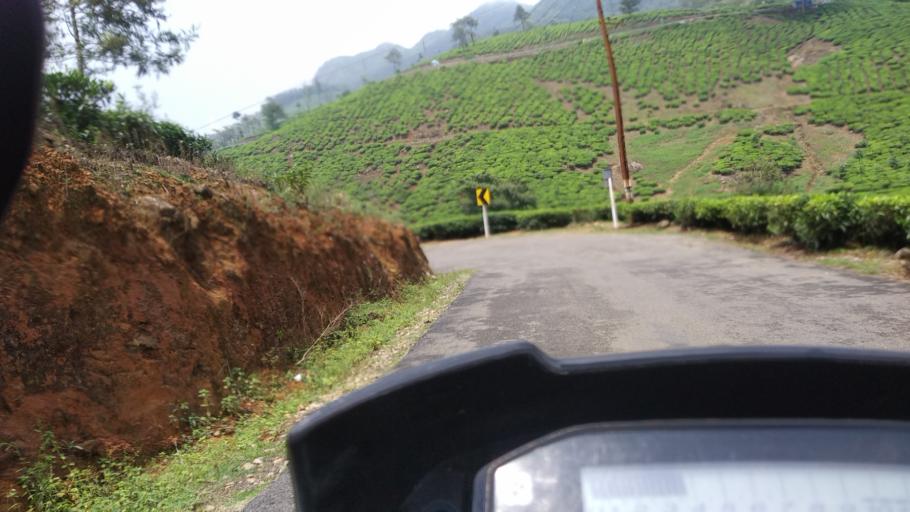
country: IN
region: Kerala
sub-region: Kottayam
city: Erattupetta
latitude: 9.6258
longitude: 76.9738
